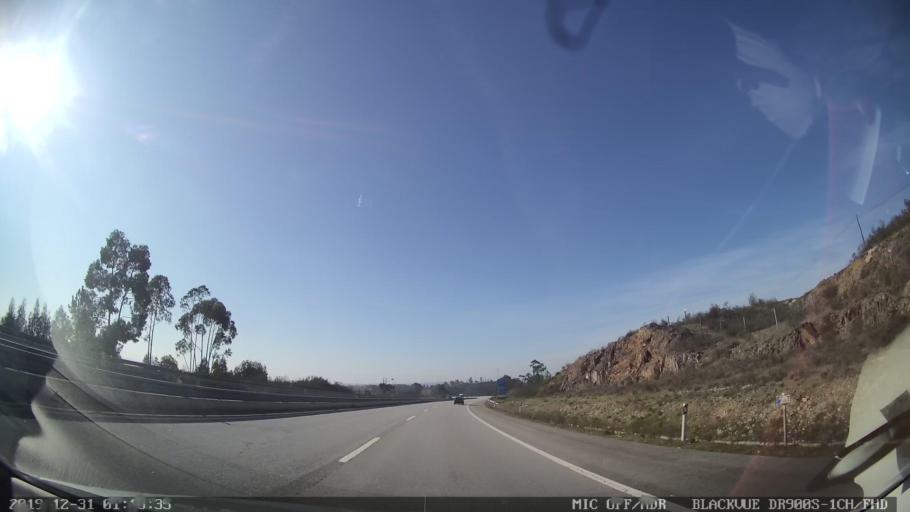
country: PT
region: Portalegre
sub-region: Nisa
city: Nisa
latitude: 39.5672
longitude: -7.7903
